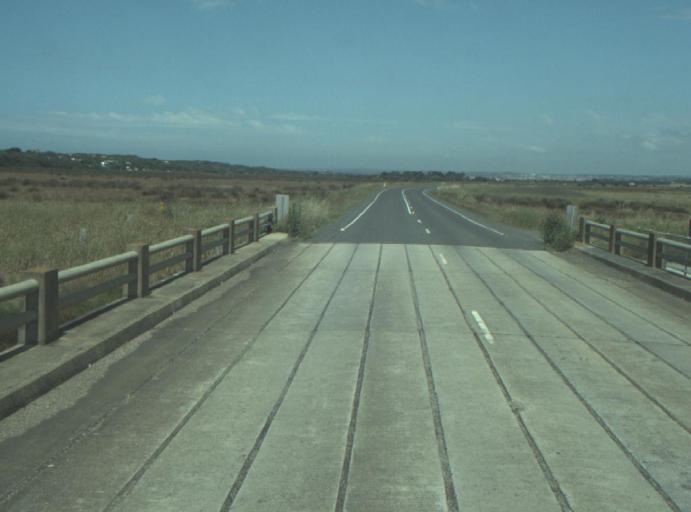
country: AU
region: Victoria
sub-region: Greater Geelong
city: Breakwater
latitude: -38.2869
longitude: 144.3969
